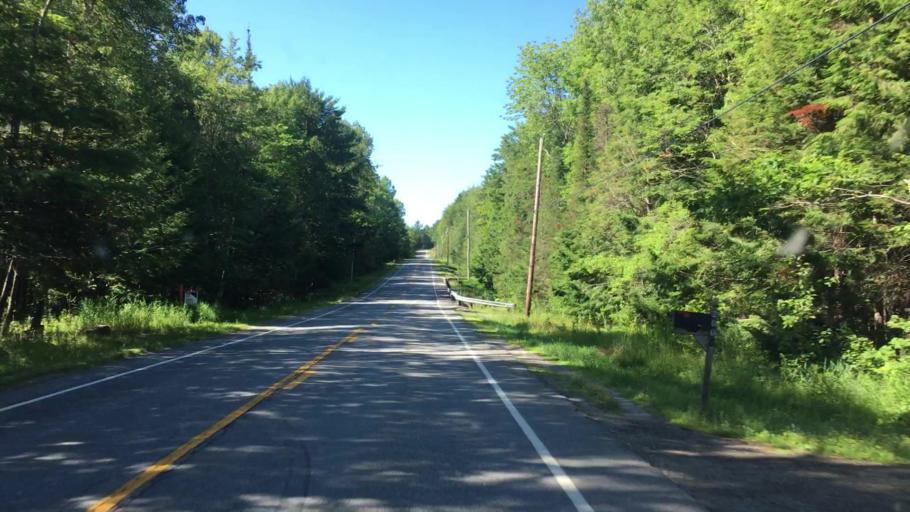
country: US
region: Maine
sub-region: Hancock County
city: Dedham
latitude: 44.6828
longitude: -68.6664
